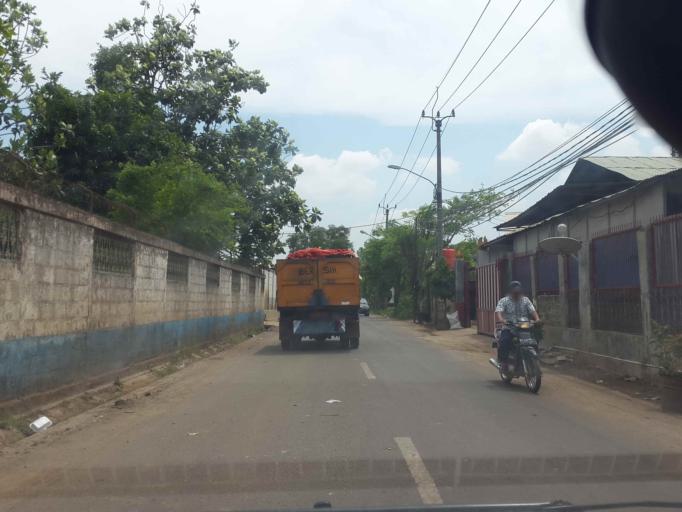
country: ID
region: Banten
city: Tangerang
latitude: -6.1435
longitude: 106.6185
